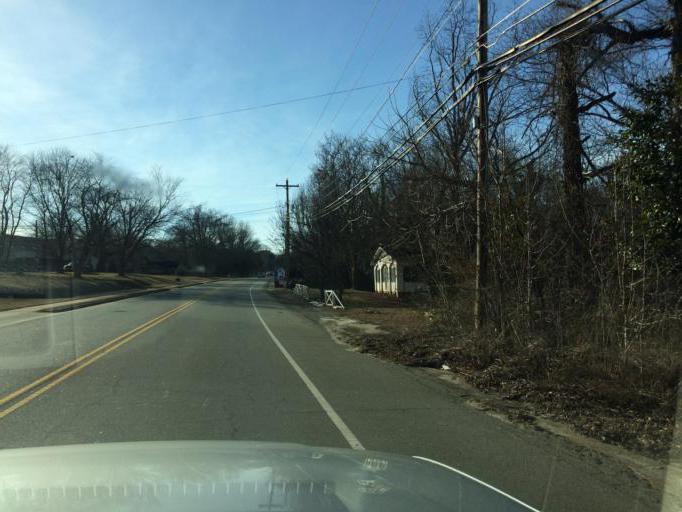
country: US
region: North Carolina
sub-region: Rutherford County
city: Forest City
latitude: 35.3322
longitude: -81.8497
